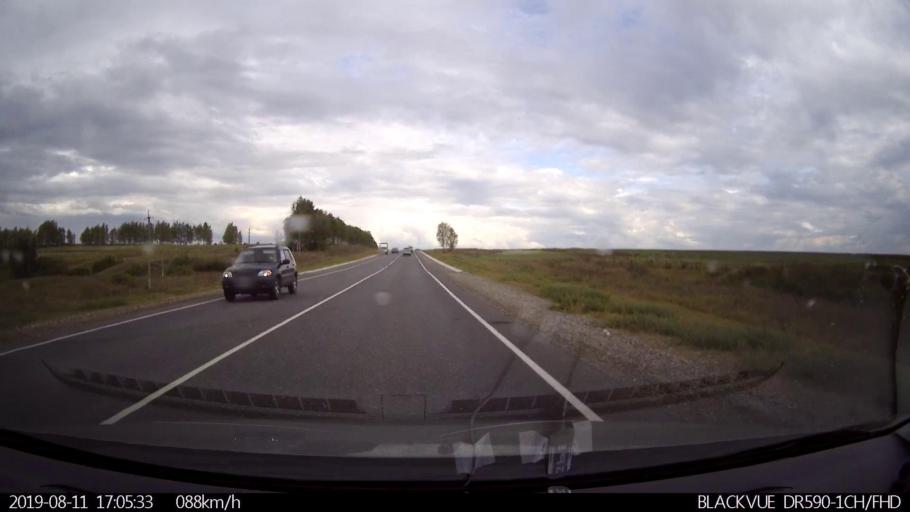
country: RU
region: Ulyanovsk
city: Mayna
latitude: 54.2979
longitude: 47.7884
